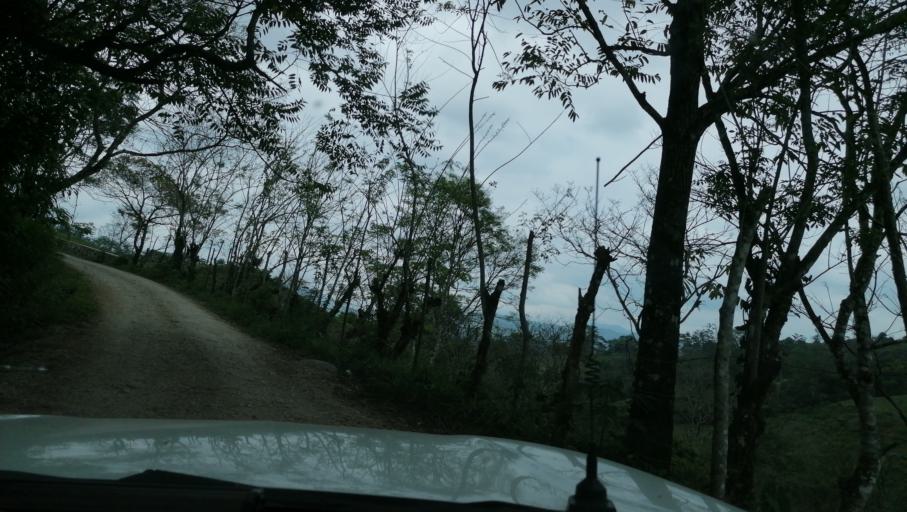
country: MX
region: Chiapas
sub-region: Ocotepec
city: San Pablo Huacano
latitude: 17.2762
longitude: -93.2323
